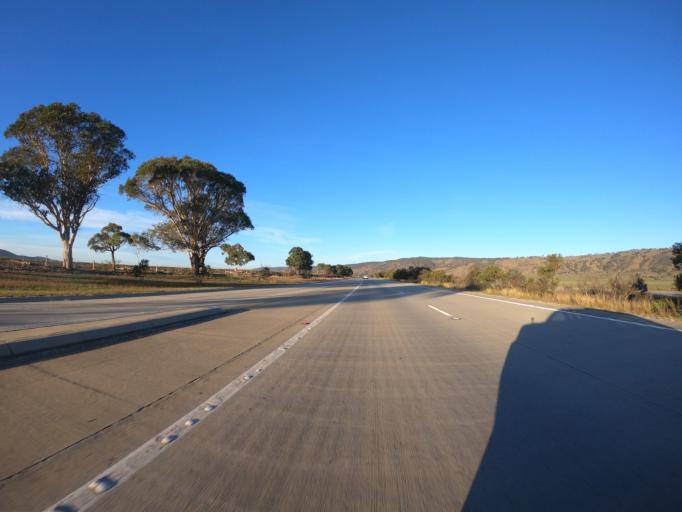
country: AU
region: New South Wales
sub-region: Yass Valley
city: Gundaroo
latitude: -34.9686
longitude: 149.4007
